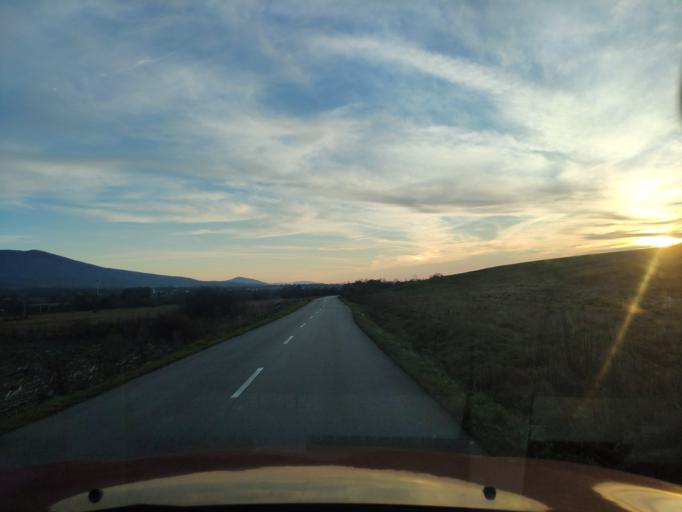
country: SK
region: Kosicky
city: Kosice
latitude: 48.6709
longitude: 21.4045
